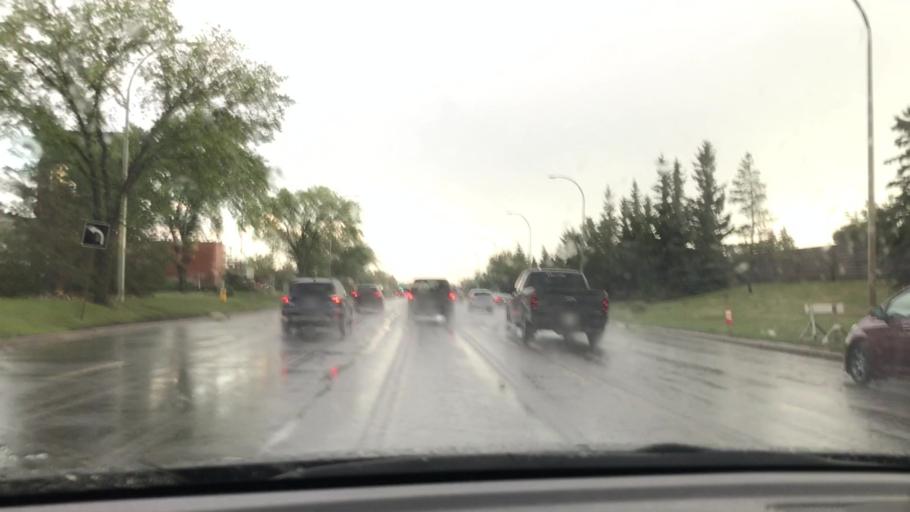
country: CA
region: Alberta
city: Edmonton
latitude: 53.4717
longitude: -113.4957
